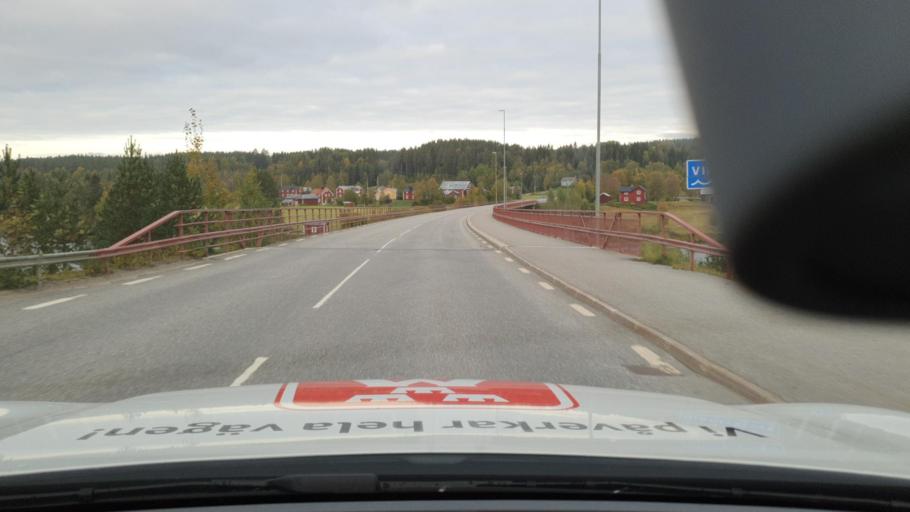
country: SE
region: Vaesterbotten
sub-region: Vindelns Kommun
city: Vindeln
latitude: 64.2009
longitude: 19.7030
